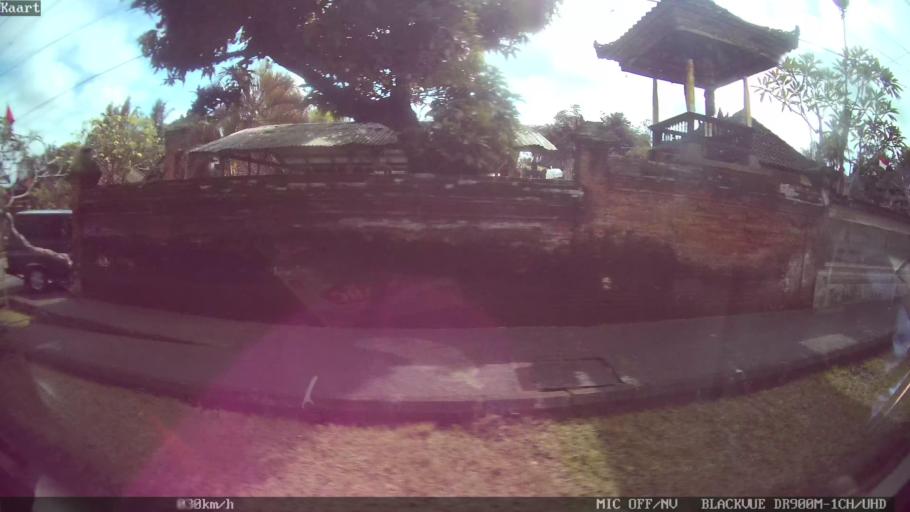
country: ID
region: Bali
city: Banjar Pesalakan
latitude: -8.5182
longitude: 115.3031
